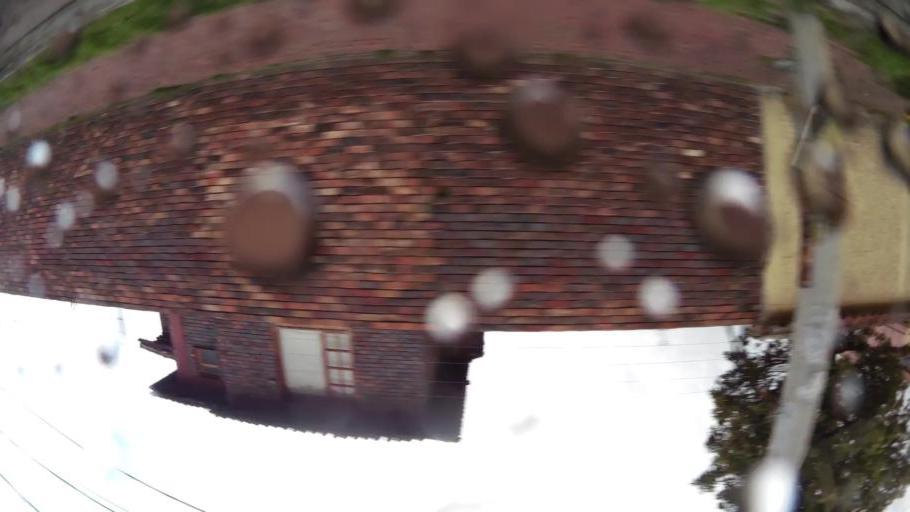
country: CO
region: Cundinamarca
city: Chia
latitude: 4.8675
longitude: -74.0450
